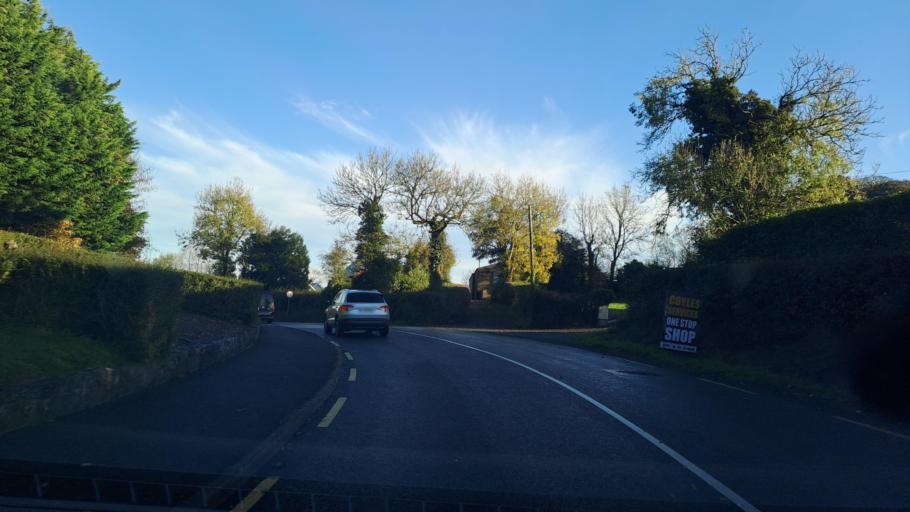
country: IE
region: Ulster
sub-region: An Cabhan
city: Cootehill
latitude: 54.1208
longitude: -7.0088
